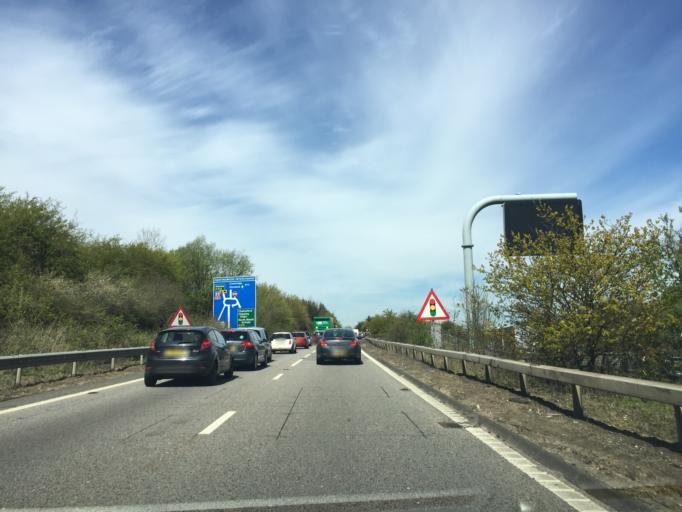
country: GB
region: England
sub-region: Essex
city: Harlow
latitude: 51.7399
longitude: 0.1363
